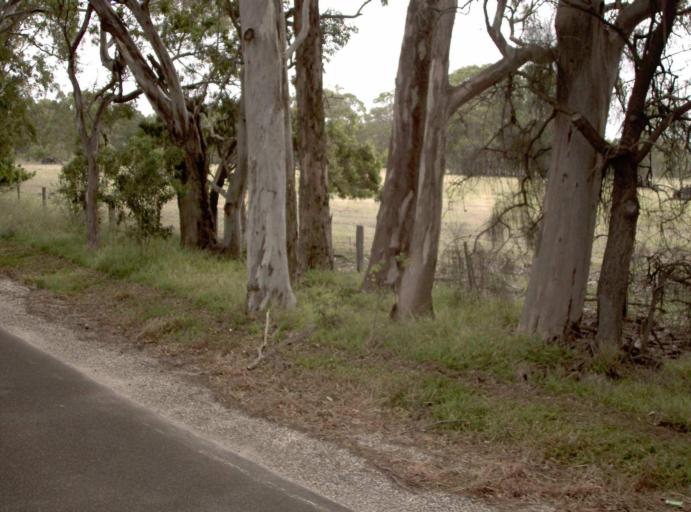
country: AU
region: Victoria
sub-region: Wellington
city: Sale
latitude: -37.8664
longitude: 147.0681
